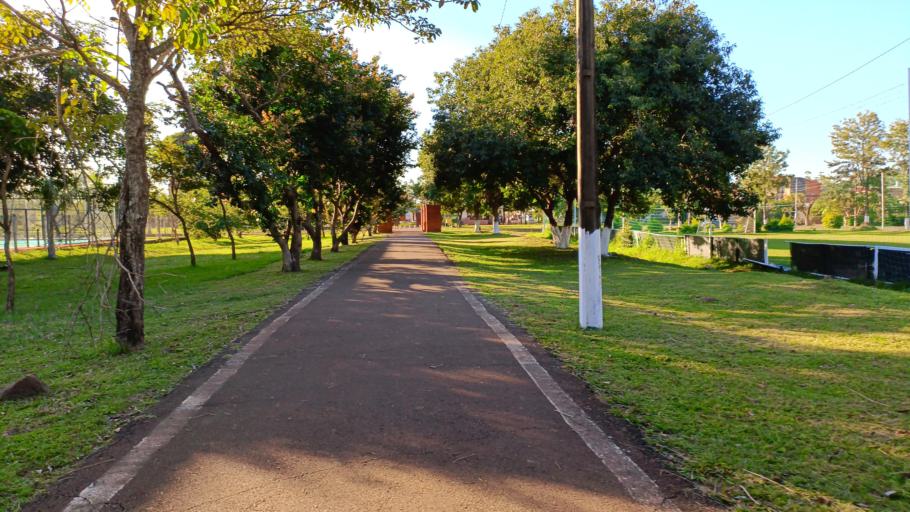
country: PY
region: Itapua
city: Carmen del Parana
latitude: -27.1578
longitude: -56.2404
